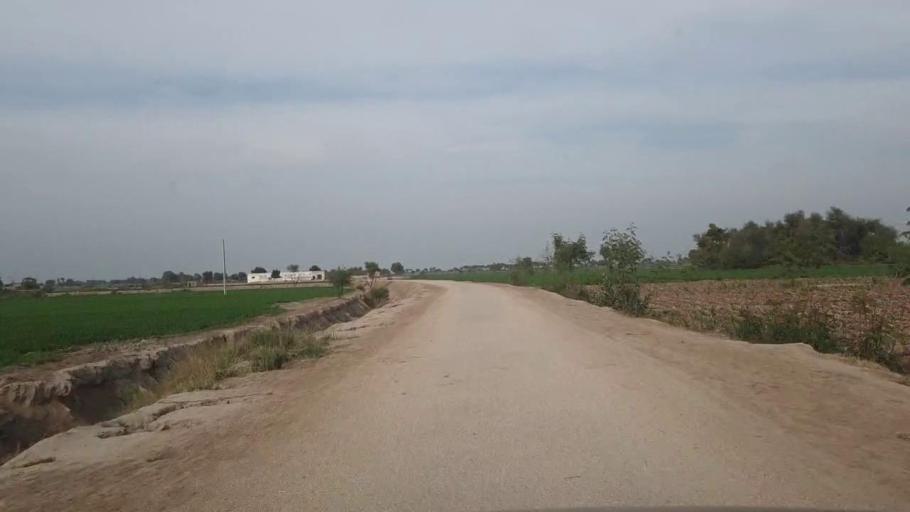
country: PK
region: Sindh
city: Shahpur Chakar
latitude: 26.1180
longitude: 68.5233
